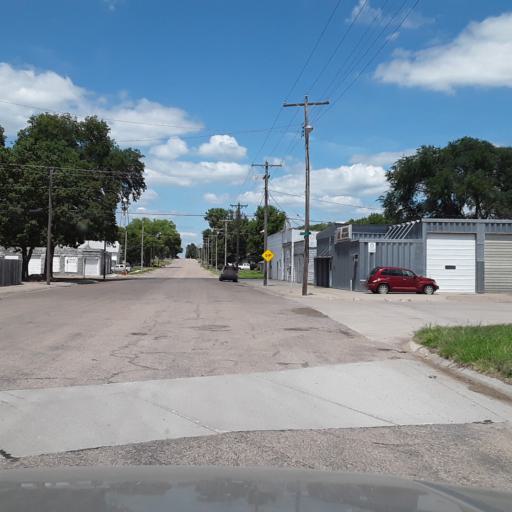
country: US
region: Nebraska
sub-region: Platte County
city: Columbus
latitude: 41.3894
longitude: -97.4933
